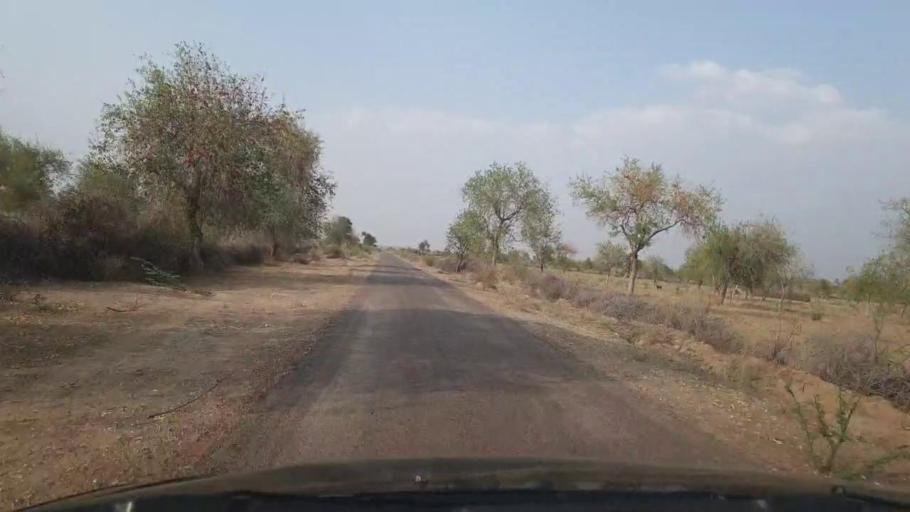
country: PK
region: Sindh
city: Islamkot
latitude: 25.0446
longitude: 70.5570
